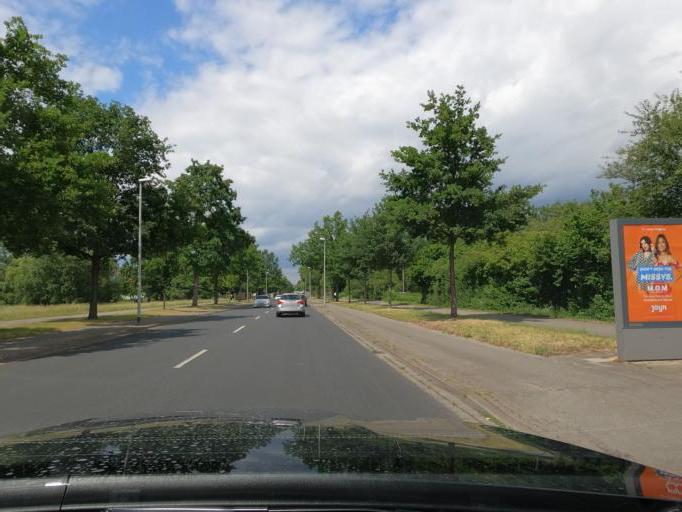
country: DE
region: Lower Saxony
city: Isernhagen Farster Bauerschaft
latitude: 52.3944
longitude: 9.8168
